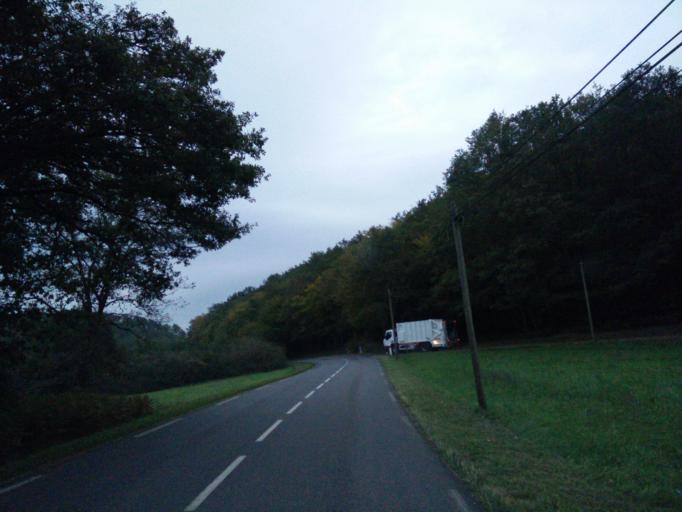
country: FR
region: Midi-Pyrenees
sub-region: Departement du Lot
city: Gourdon
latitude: 44.7727
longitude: 1.3357
